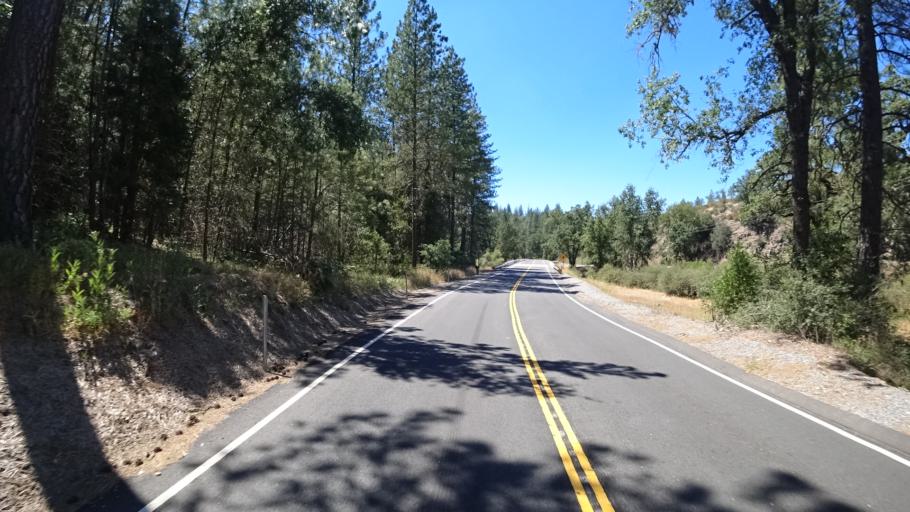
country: US
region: California
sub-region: Calaveras County
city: Mountain Ranch
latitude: 38.2952
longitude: -120.4952
